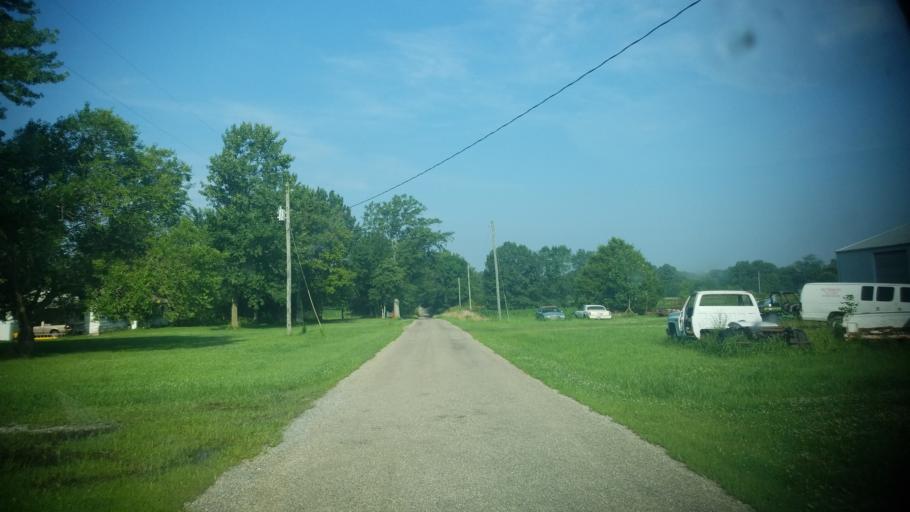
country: US
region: Illinois
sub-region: Clay County
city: Flora
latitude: 38.6028
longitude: -88.4064
